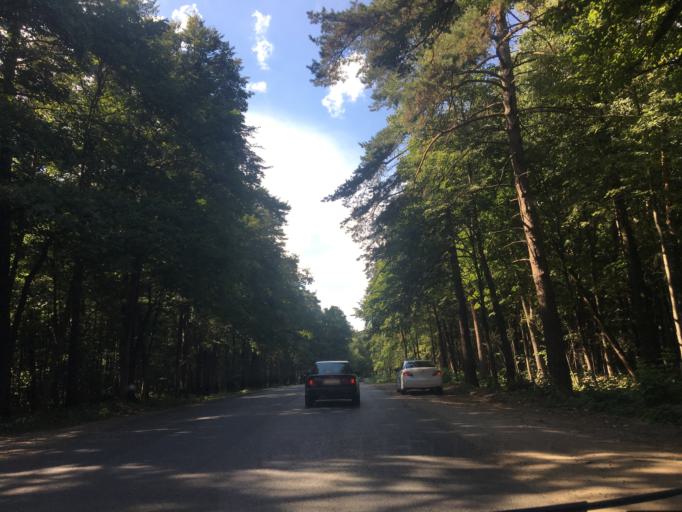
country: RU
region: Moscow
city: Zagor'ye
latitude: 55.5290
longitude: 37.6592
